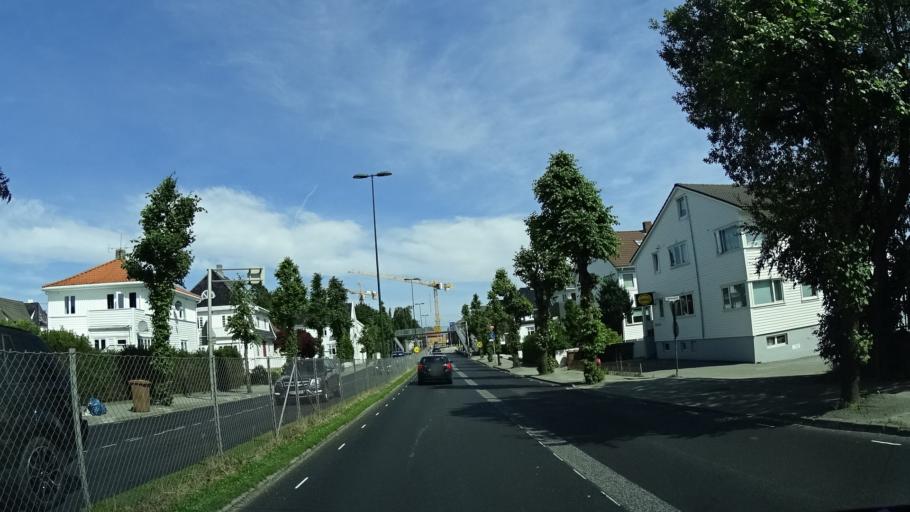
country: NO
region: Rogaland
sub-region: Stavanger
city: Stavanger
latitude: 58.9621
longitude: 5.7198
